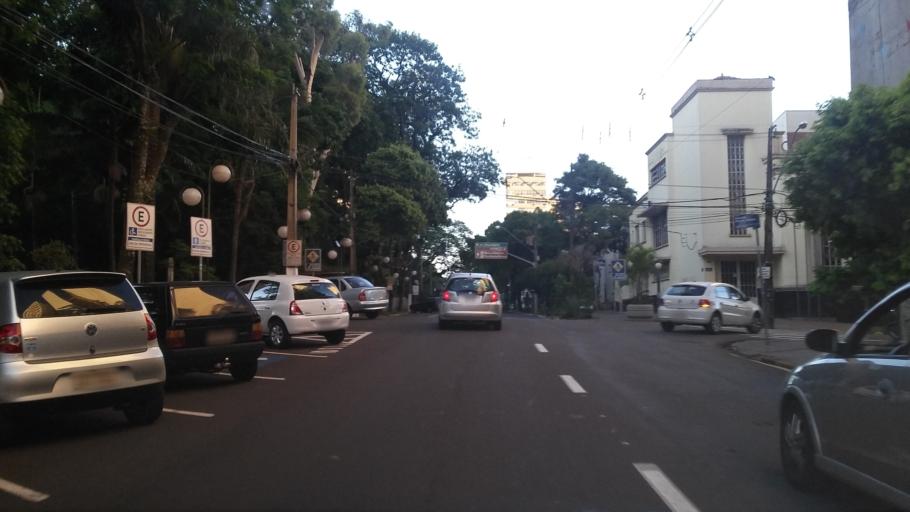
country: BR
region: Parana
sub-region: Londrina
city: Londrina
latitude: -23.3136
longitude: -51.1589
